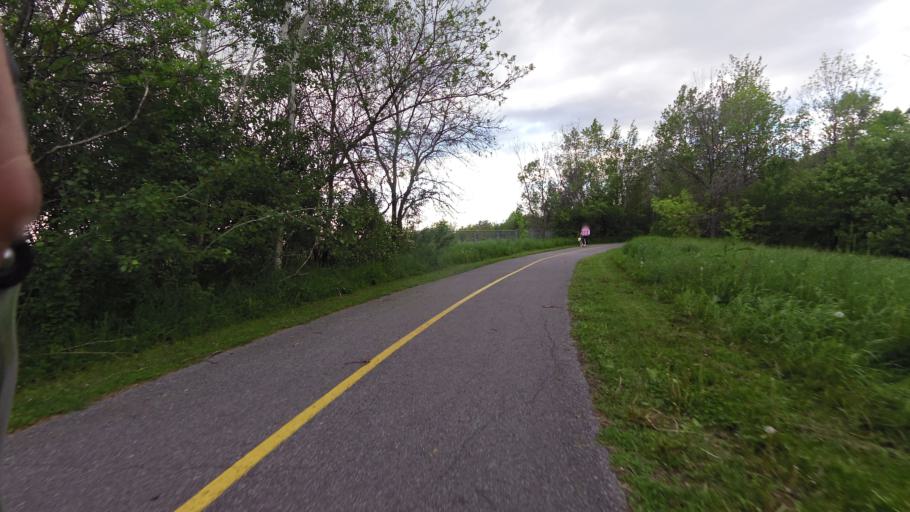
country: CA
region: Ontario
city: Bells Corners
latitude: 45.3277
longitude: -75.8888
